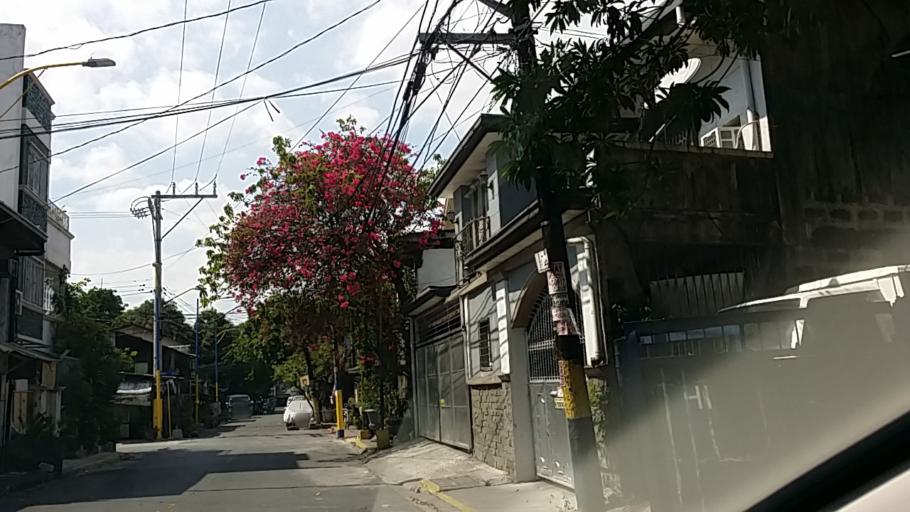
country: PH
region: Metro Manila
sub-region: Mandaluyong
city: Mandaluyong City
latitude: 14.5708
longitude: 121.0442
